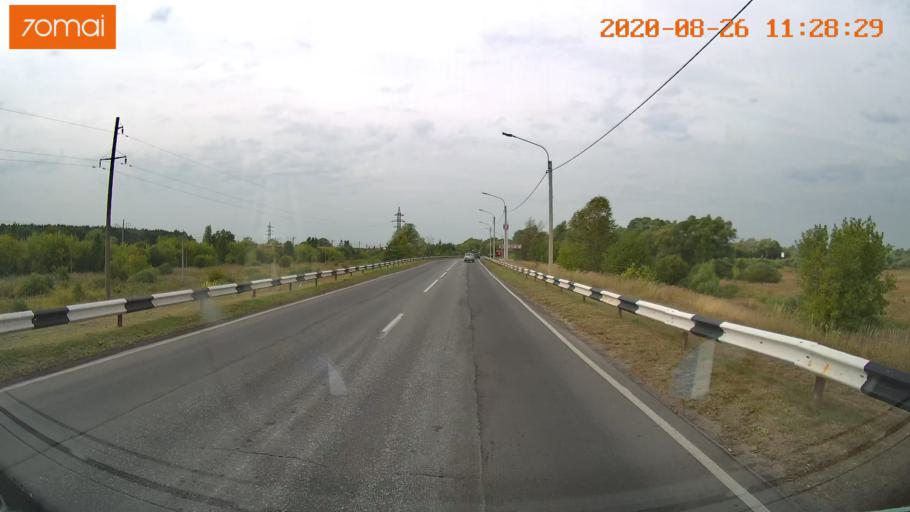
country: RU
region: Rjazan
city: Shilovo
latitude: 54.3232
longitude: 40.9122
